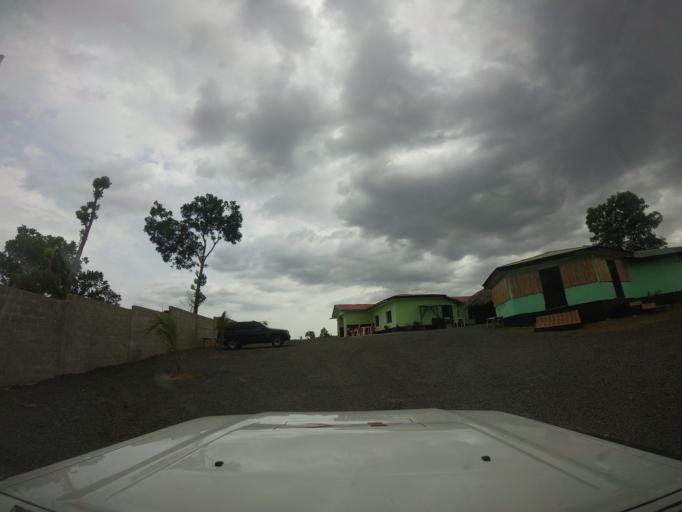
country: LR
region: Bomi
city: Tubmanburg
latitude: 6.8580
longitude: -10.8196
